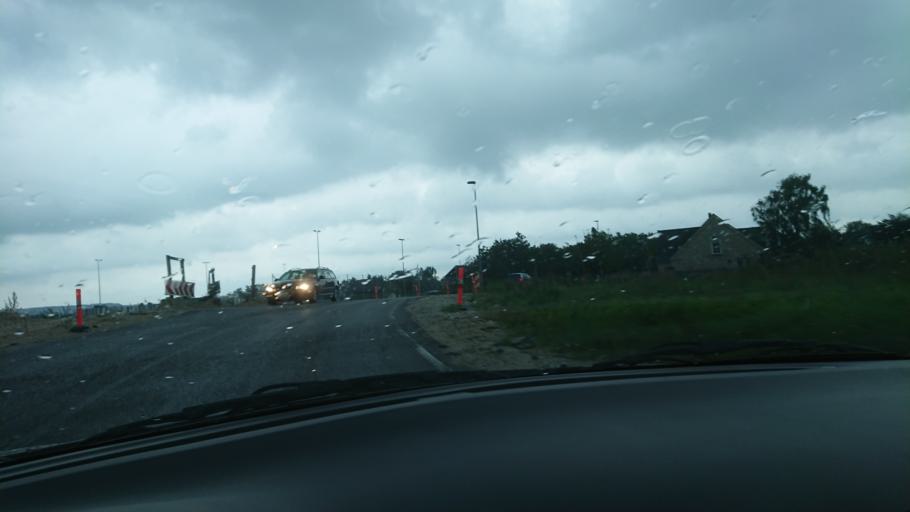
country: DK
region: North Denmark
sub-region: Alborg Kommune
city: Aalborg
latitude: 57.0035
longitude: 9.9217
